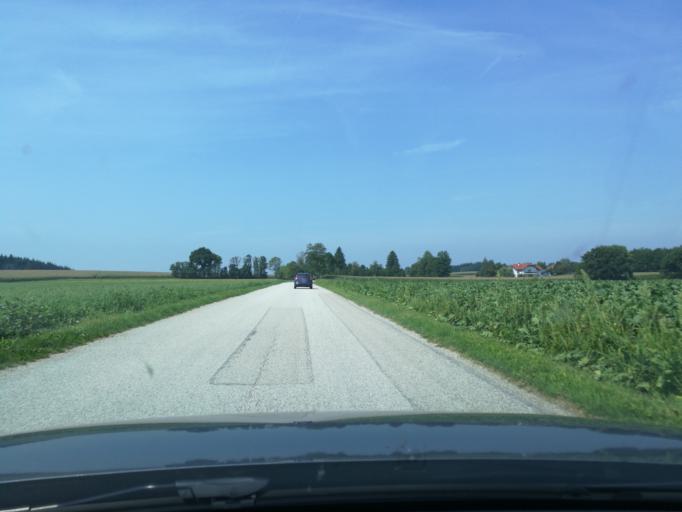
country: AT
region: Upper Austria
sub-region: Politischer Bezirk Grieskirchen
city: Grieskirchen
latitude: 48.2893
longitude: 13.8074
